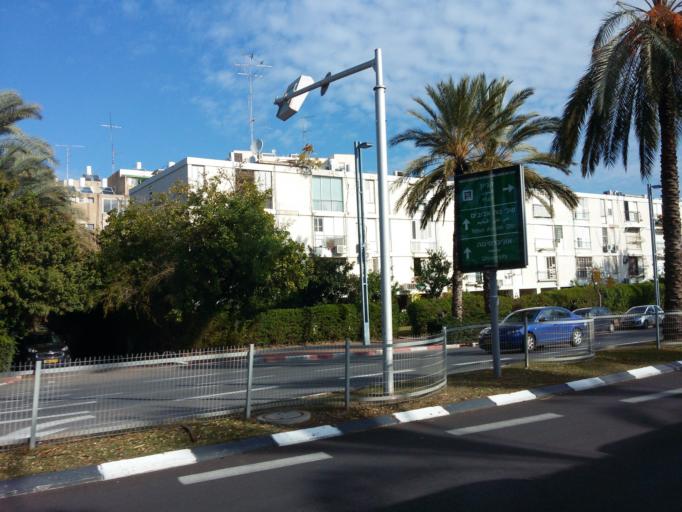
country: IL
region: Tel Aviv
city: Tel Aviv
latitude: 32.1126
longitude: 34.7925
